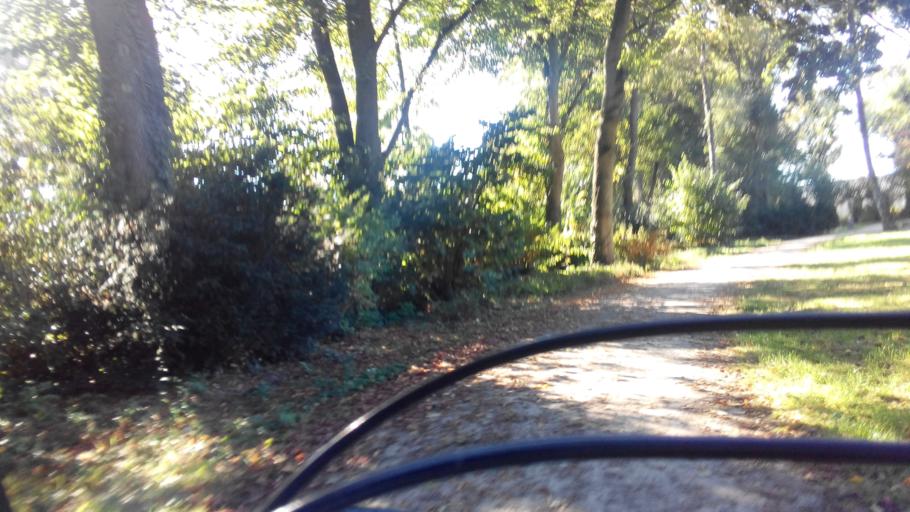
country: DE
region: North Rhine-Westphalia
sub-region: Regierungsbezirk Munster
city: Gelsenkirchen
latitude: 51.4992
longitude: 7.1260
